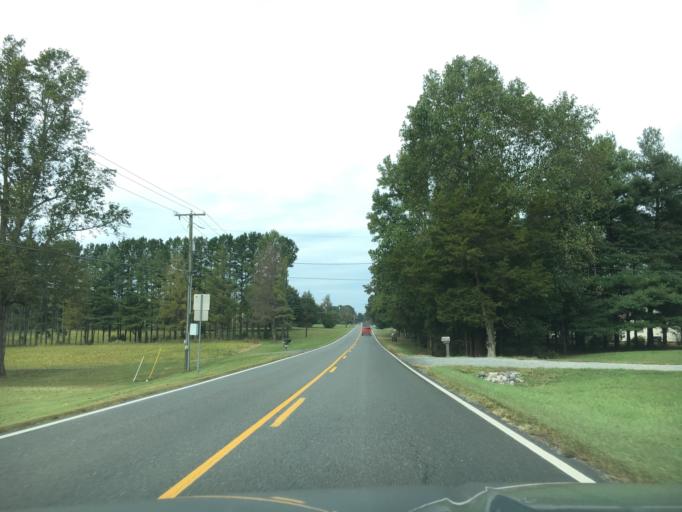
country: US
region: Virginia
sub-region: Goochland County
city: Goochland
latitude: 37.7238
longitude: -77.8298
